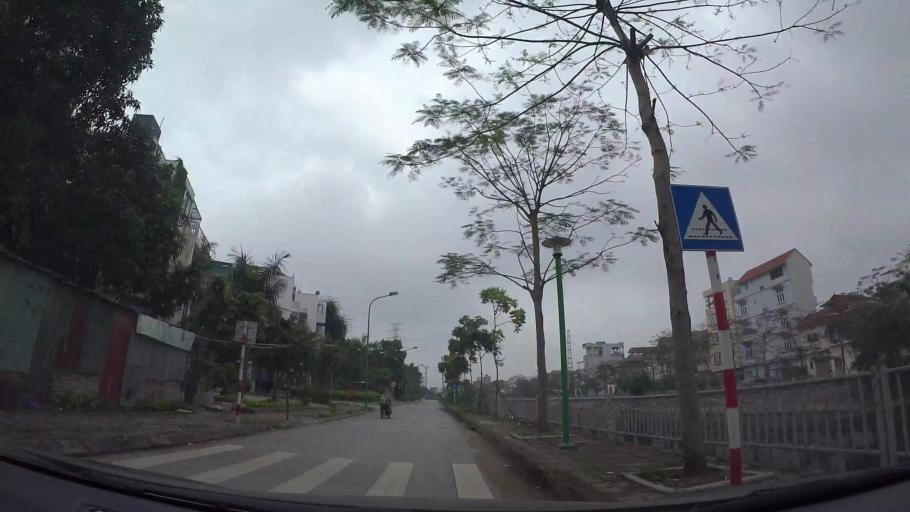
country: VN
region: Ha Noi
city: Van Dien
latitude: 20.9739
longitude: 105.8519
